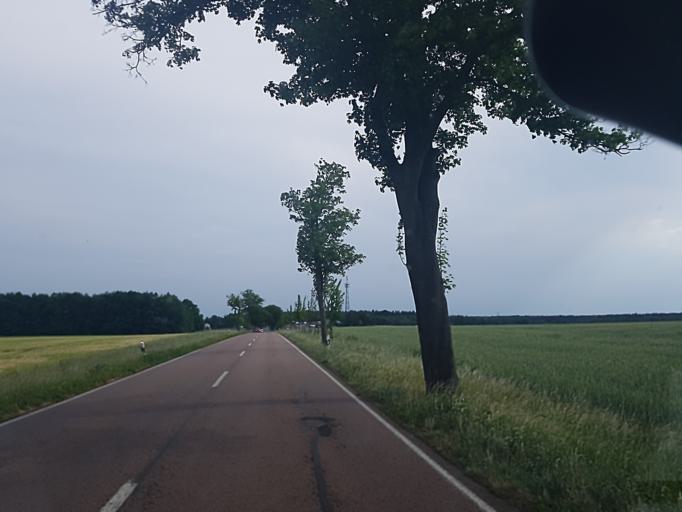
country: DE
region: Saxony-Anhalt
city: Nudersdorf
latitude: 51.9163
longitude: 12.6061
